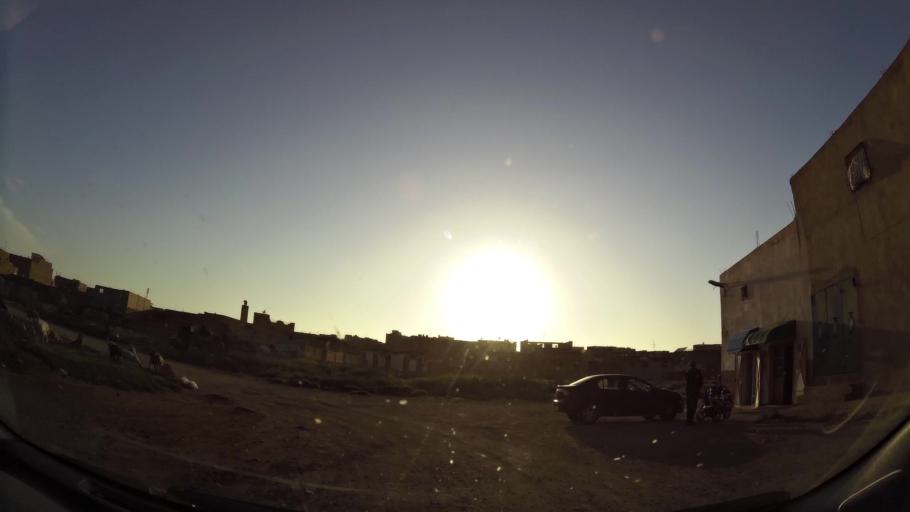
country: MA
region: Oriental
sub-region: Oujda-Angad
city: Oujda
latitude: 34.7065
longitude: -1.9086
